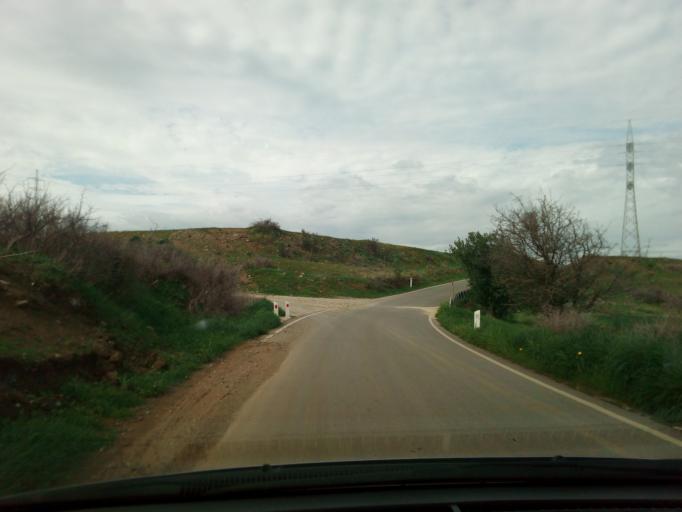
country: CY
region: Lefkosia
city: Astromeritis
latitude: 35.0957
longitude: 32.9884
